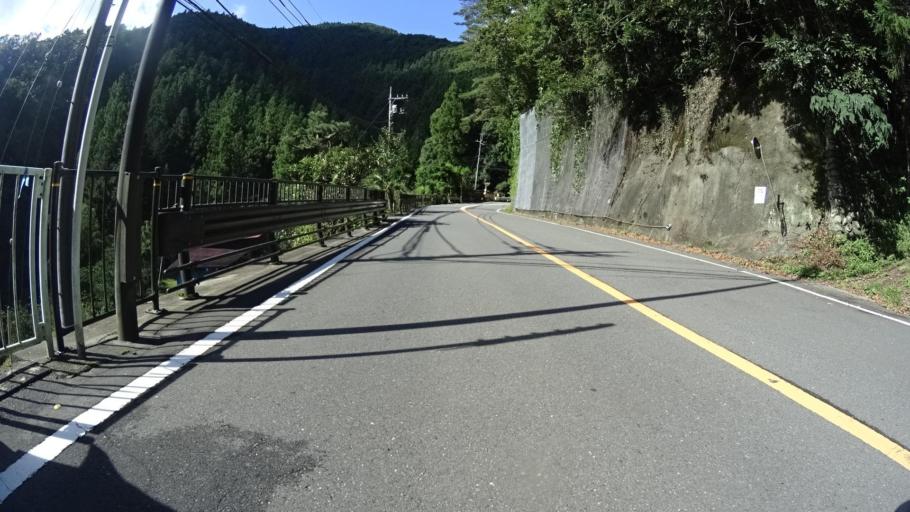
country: JP
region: Yamanashi
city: Uenohara
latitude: 35.7374
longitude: 139.0909
